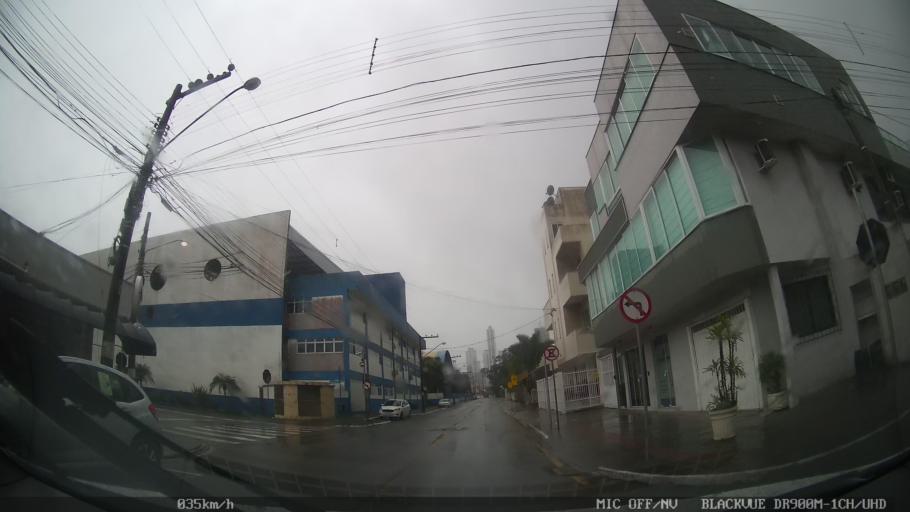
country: BR
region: Santa Catarina
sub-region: Balneario Camboriu
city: Balneario Camboriu
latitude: -27.0104
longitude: -48.6262
